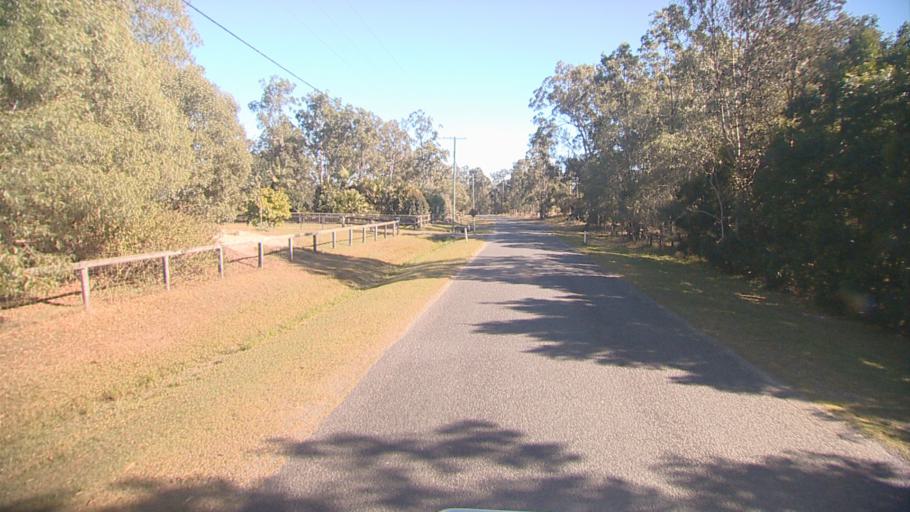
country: AU
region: Queensland
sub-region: Logan
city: Chambers Flat
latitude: -27.7869
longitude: 153.1299
